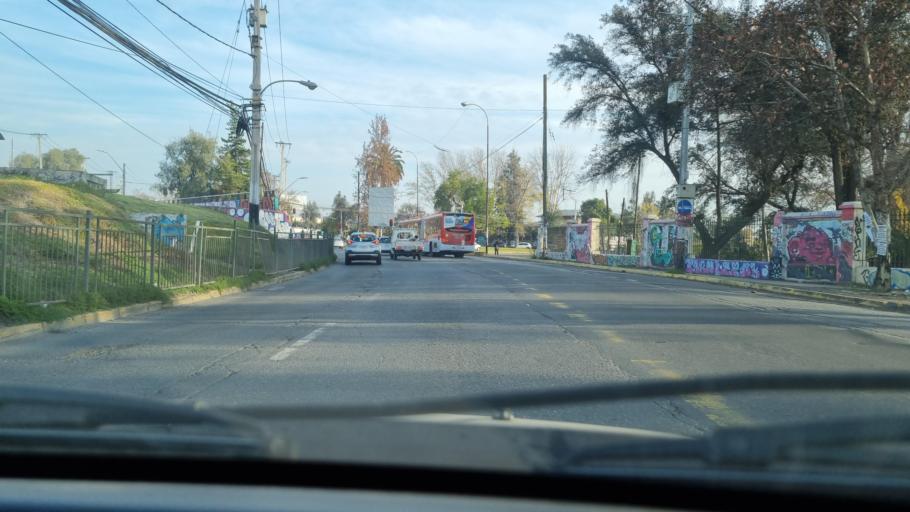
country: CL
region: Santiago Metropolitan
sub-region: Provincia de Santiago
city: Lo Prado
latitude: -33.4933
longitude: -70.7568
